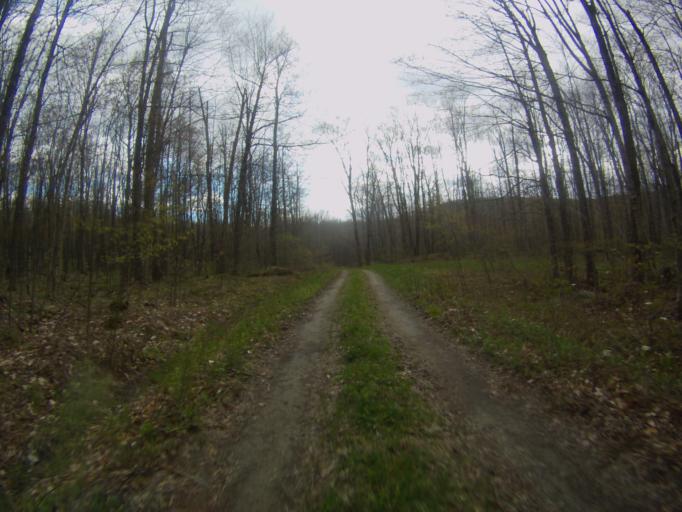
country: US
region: Vermont
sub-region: Addison County
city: Bristol
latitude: 44.0501
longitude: -73.0514
